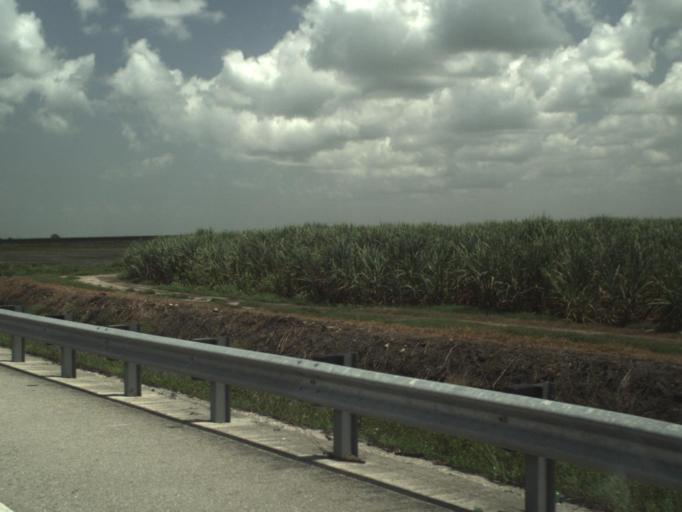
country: US
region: Florida
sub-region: Palm Beach County
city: Pahokee
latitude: 26.7541
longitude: -80.6598
